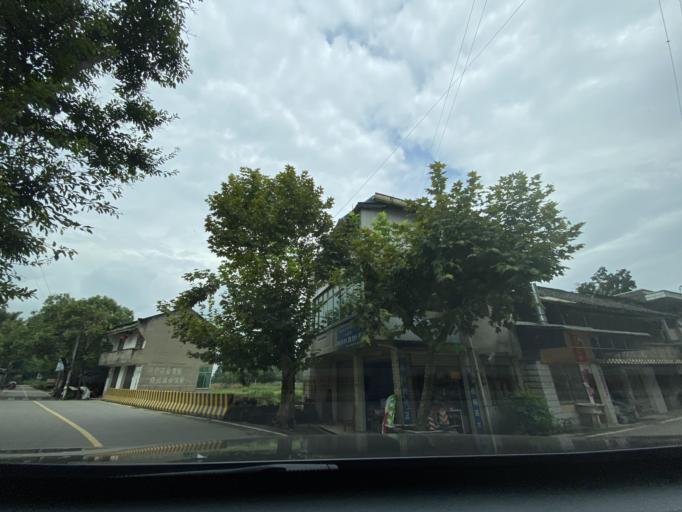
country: CN
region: Sichuan
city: Wujin
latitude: 30.3701
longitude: 103.9691
